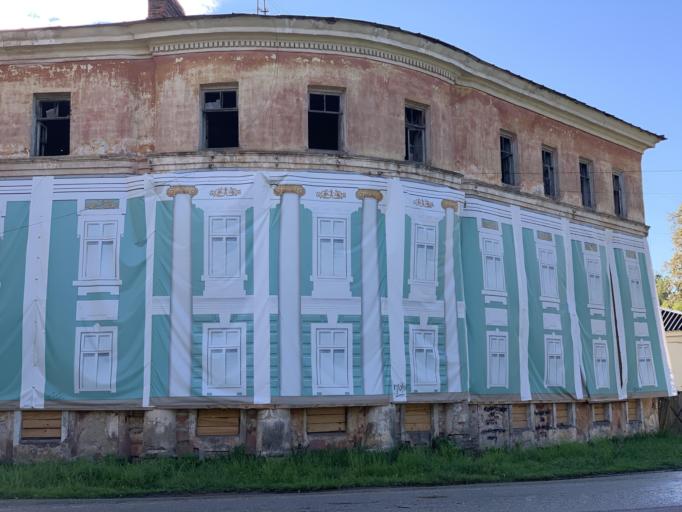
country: RU
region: Tverskaya
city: Vyshniy Volochek
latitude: 57.5861
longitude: 34.5501
